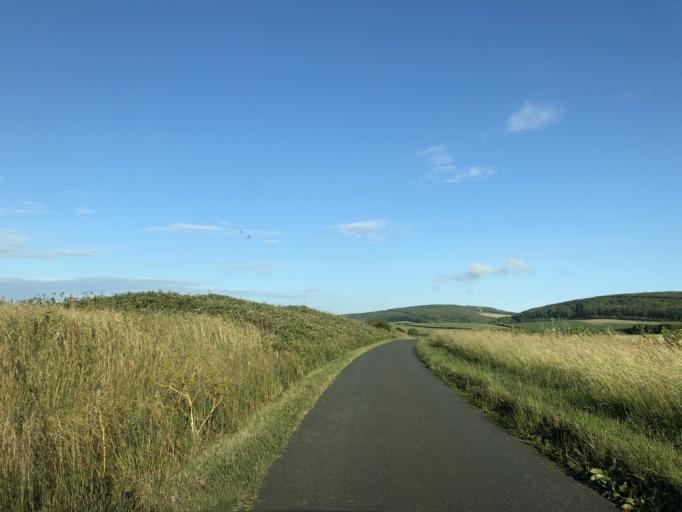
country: GB
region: England
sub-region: Isle of Wight
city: Yarmouth
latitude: 50.6783
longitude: -1.4594
